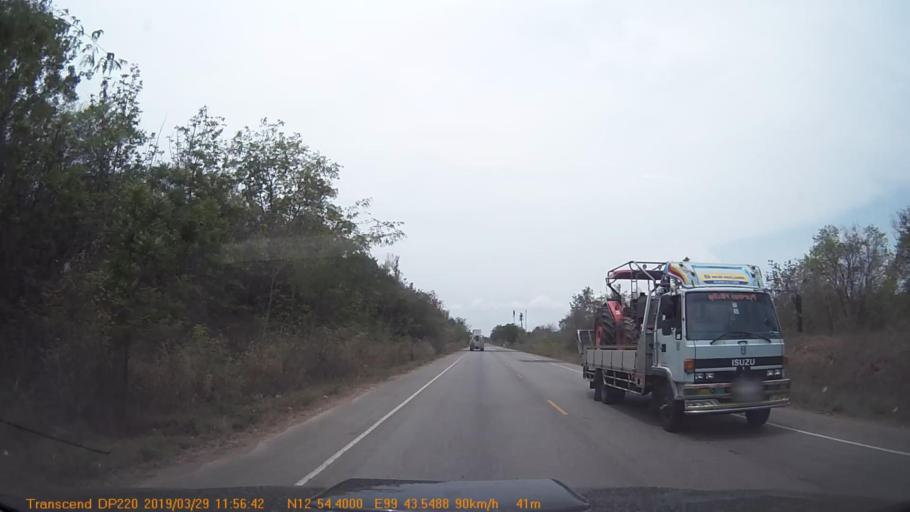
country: TH
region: Phetchaburi
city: Kaeng Krachan
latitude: 12.9063
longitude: 99.7255
